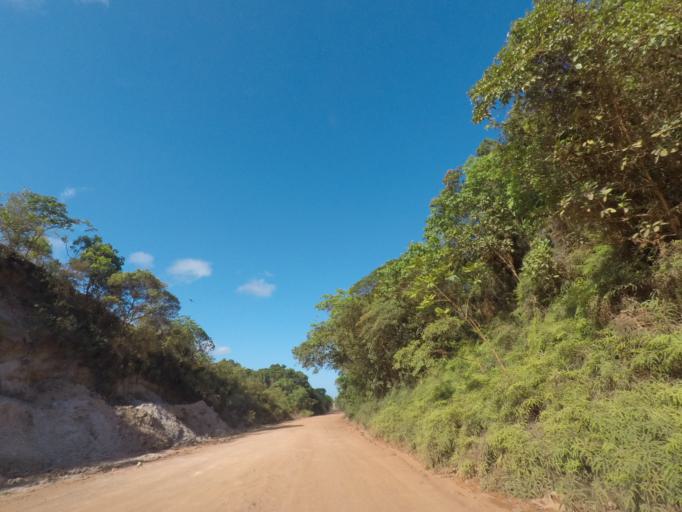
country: BR
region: Bahia
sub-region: Marau
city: Marau
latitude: -14.1294
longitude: -38.9940
